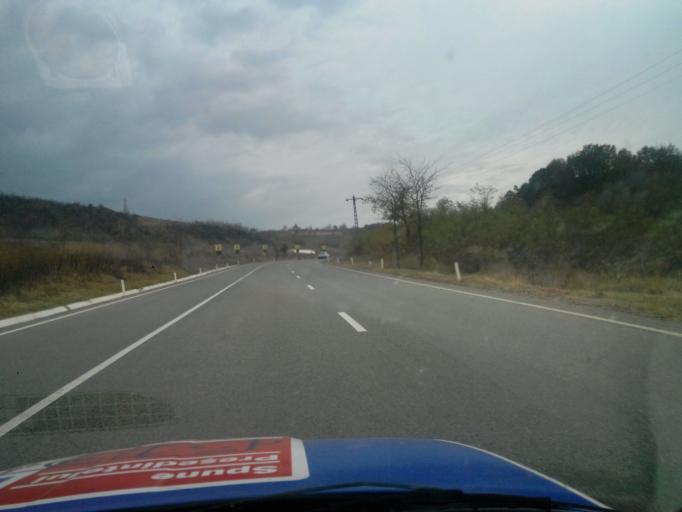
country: RO
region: Vaslui
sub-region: Comuna Duda  Epureni
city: Epureni
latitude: 46.6806
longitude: 28.0143
